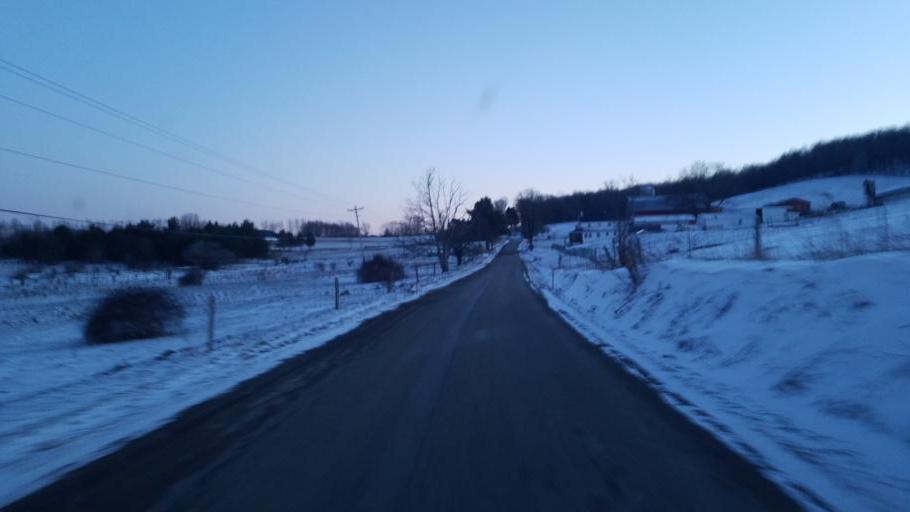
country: US
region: New York
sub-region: Allegany County
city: Andover
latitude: 41.9837
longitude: -77.7617
